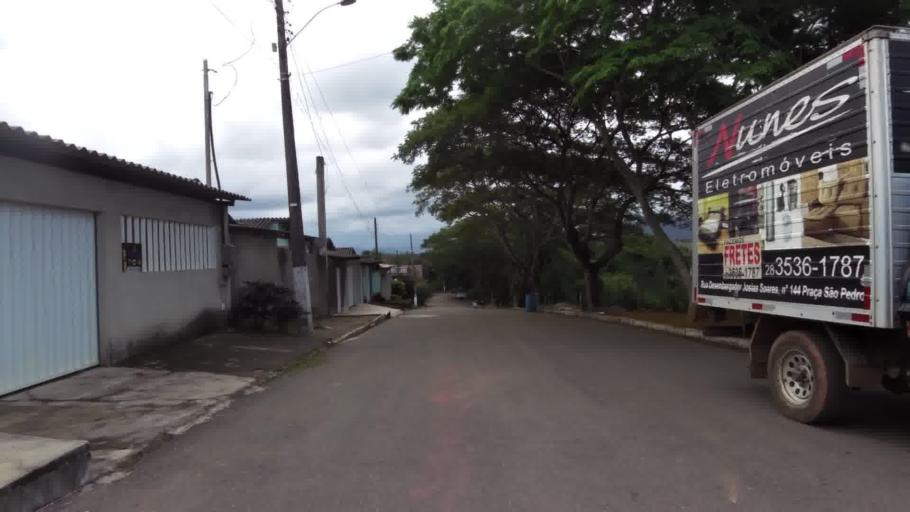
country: BR
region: Espirito Santo
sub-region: Piuma
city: Piuma
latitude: -20.7931
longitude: -40.6376
